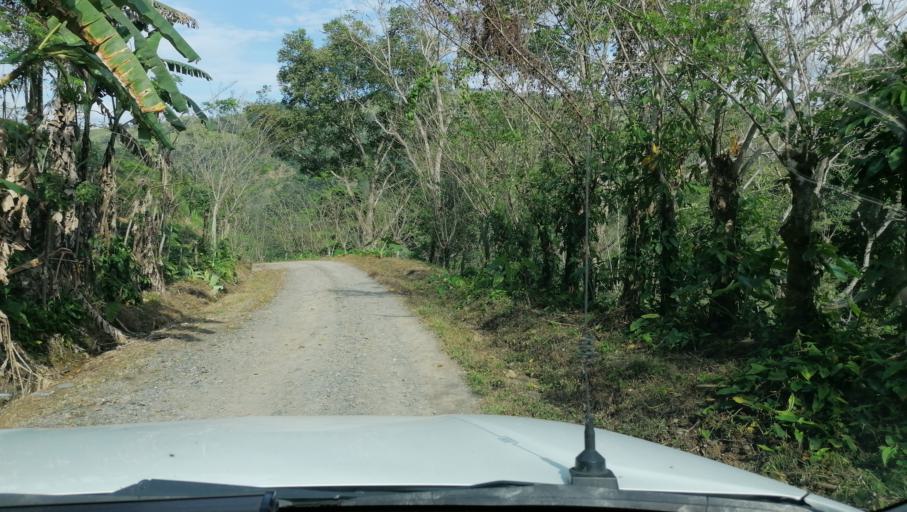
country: MX
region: Chiapas
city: Ostuacan
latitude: 17.4535
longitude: -93.2445
